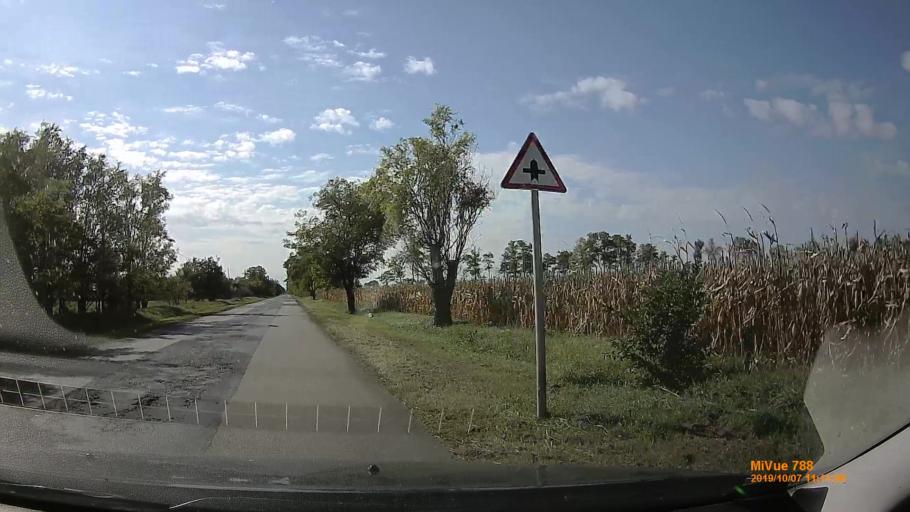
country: HU
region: Bekes
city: Kondoros
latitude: 46.7310
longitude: 20.7808
